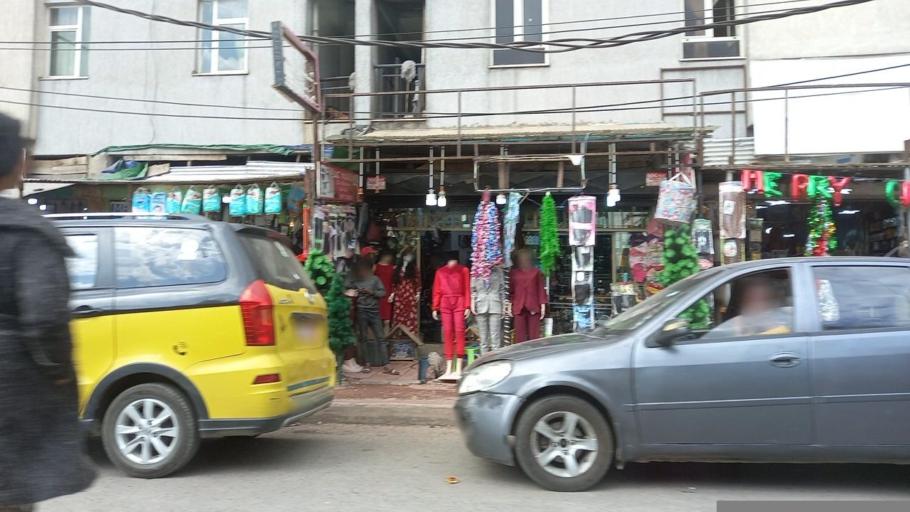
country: ET
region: Adis Abeba
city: Addis Ababa
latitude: 9.0100
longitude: 38.8531
